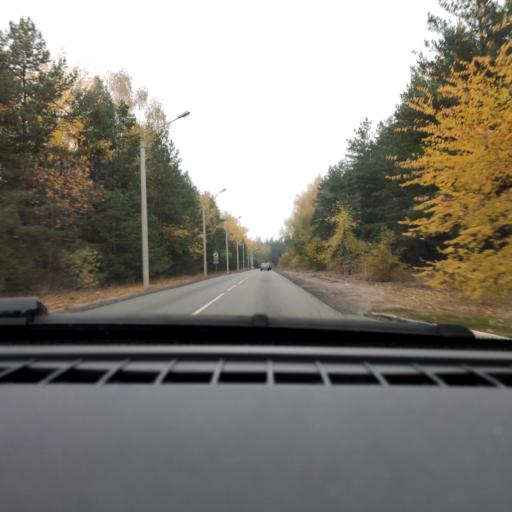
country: RU
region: Voronezj
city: Somovo
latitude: 51.7095
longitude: 39.3261
